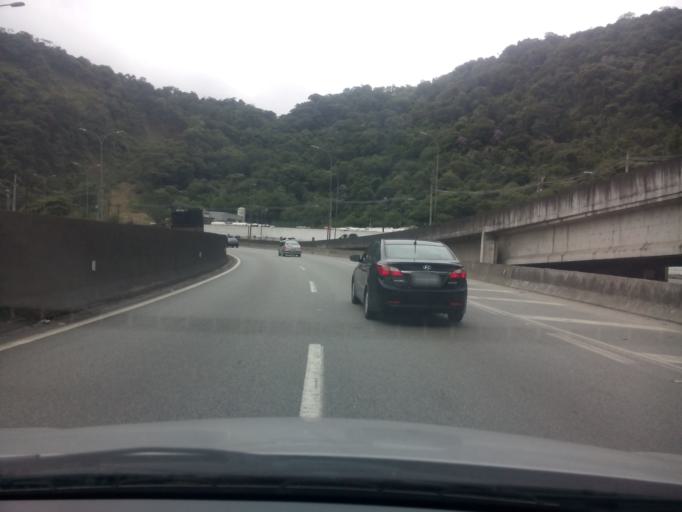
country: BR
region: Sao Paulo
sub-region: Cubatao
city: Cubatao
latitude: -23.8894
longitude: -46.4410
